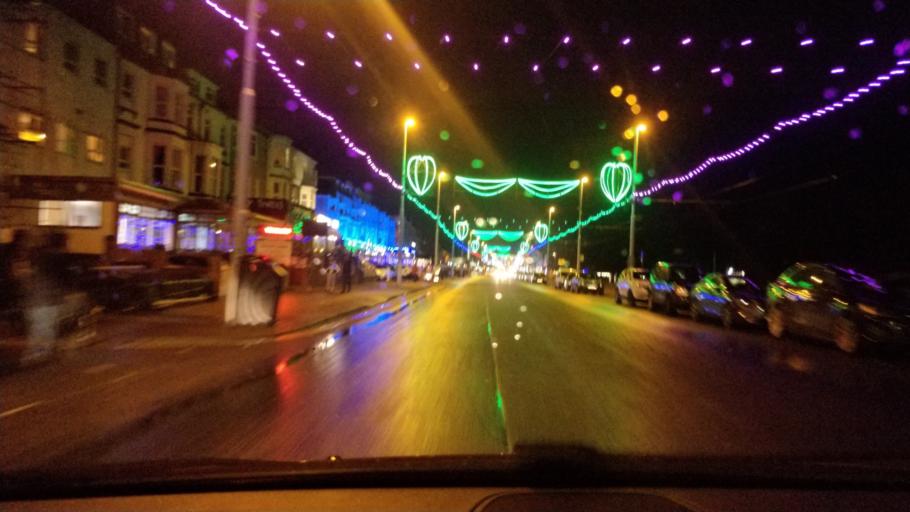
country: GB
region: England
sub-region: Blackpool
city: Blackpool
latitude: 53.8049
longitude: -3.0552
